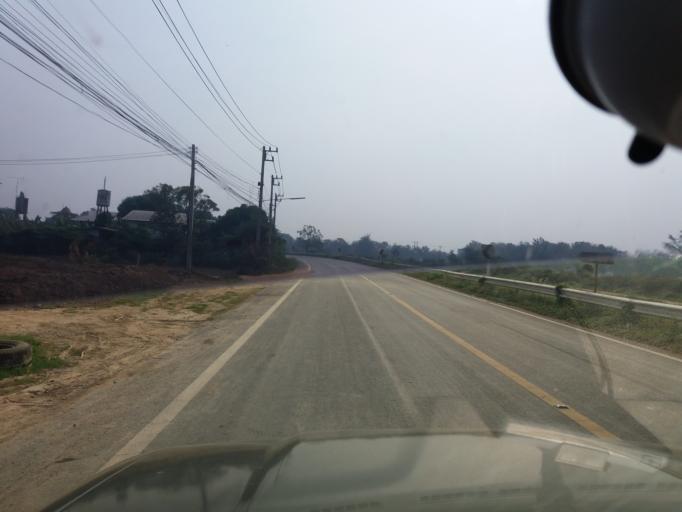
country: TH
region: Suphan Buri
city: Doem Bang Nang Buat
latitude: 14.9045
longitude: 100.1936
